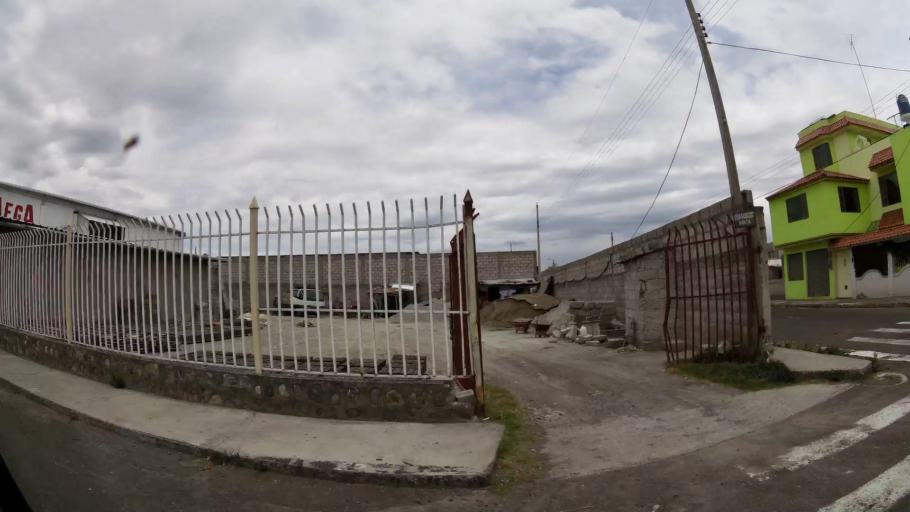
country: EC
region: Cotopaxi
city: San Miguel de Salcedo
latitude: -1.0368
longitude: -78.5901
